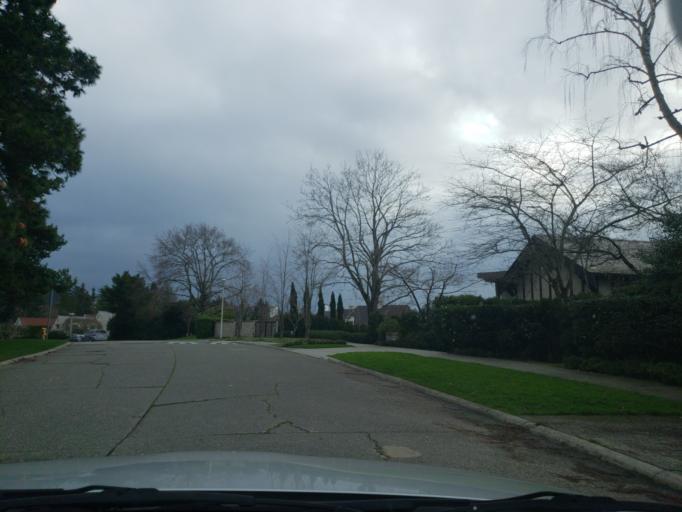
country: US
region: Washington
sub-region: King County
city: Medina
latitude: 47.6561
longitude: -122.2858
